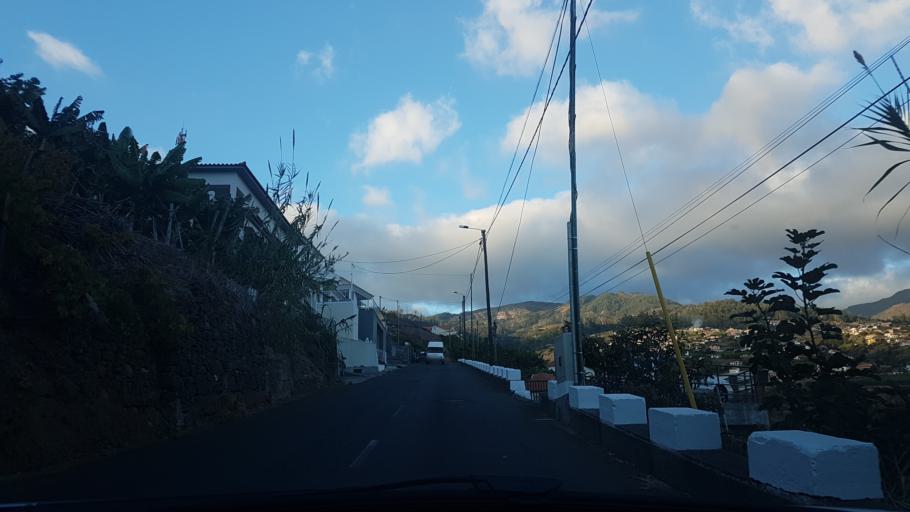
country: PT
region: Madeira
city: Ponta do Sol
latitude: 32.6880
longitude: -17.1107
